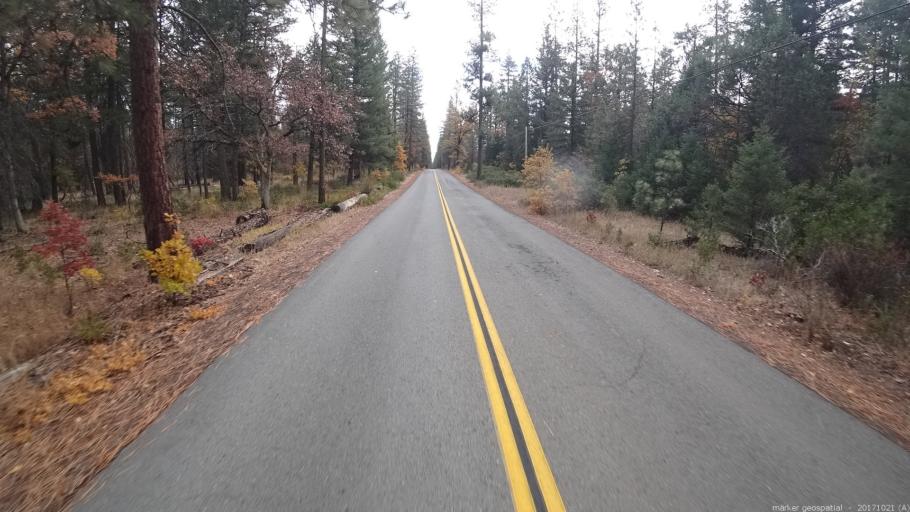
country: US
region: California
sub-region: Shasta County
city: Burney
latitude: 41.0061
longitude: -121.6481
